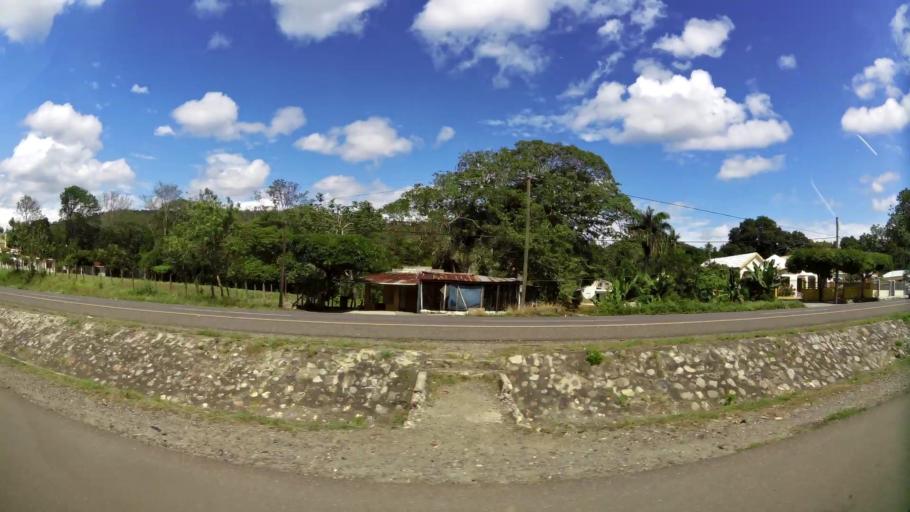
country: DO
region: La Vega
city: Rio Verde Arriba
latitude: 19.2916
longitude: -70.5763
